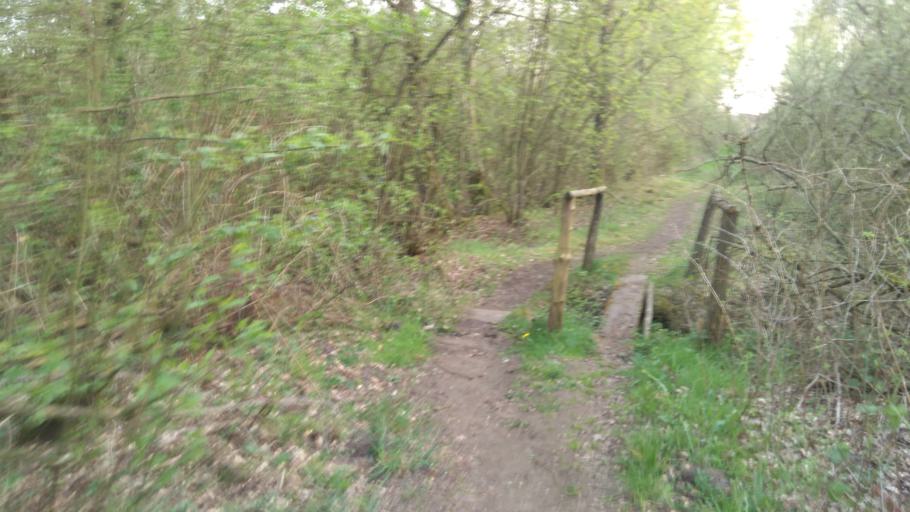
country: DE
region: Lower Saxony
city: Bliedersdorf
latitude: 53.4874
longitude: 9.5576
